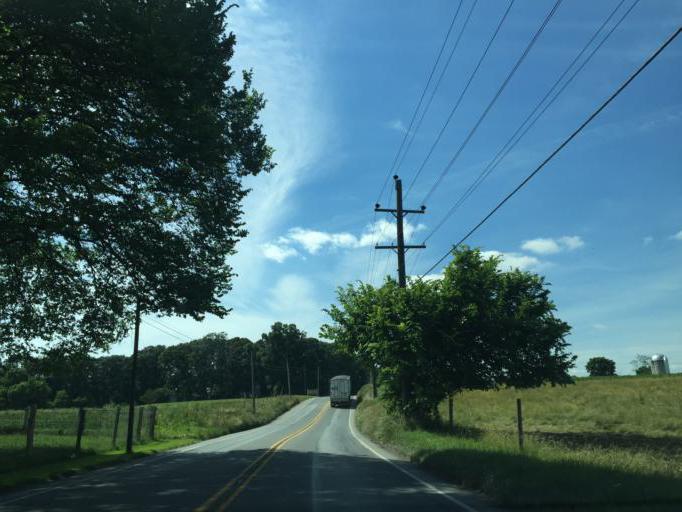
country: US
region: Pennsylvania
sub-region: York County
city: Susquehanna Trails
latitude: 39.7749
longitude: -76.3469
